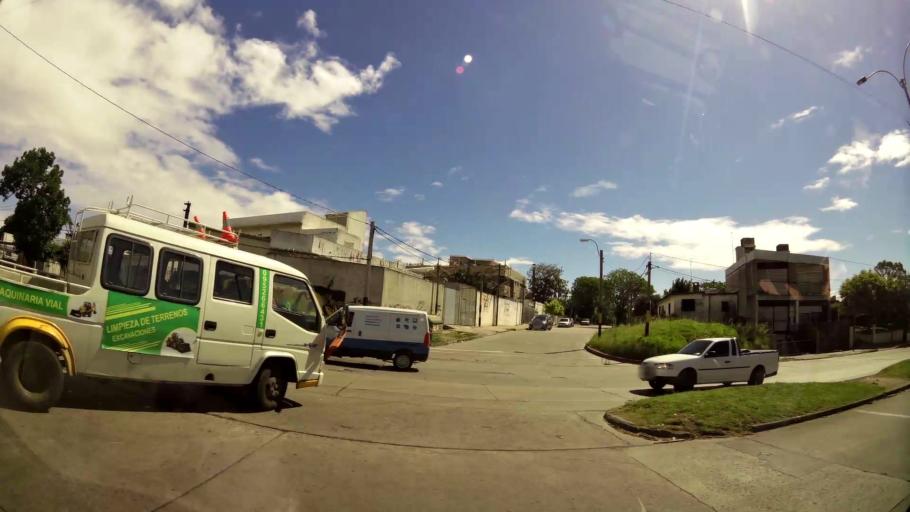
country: UY
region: Montevideo
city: Montevideo
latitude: -34.8483
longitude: -56.1877
